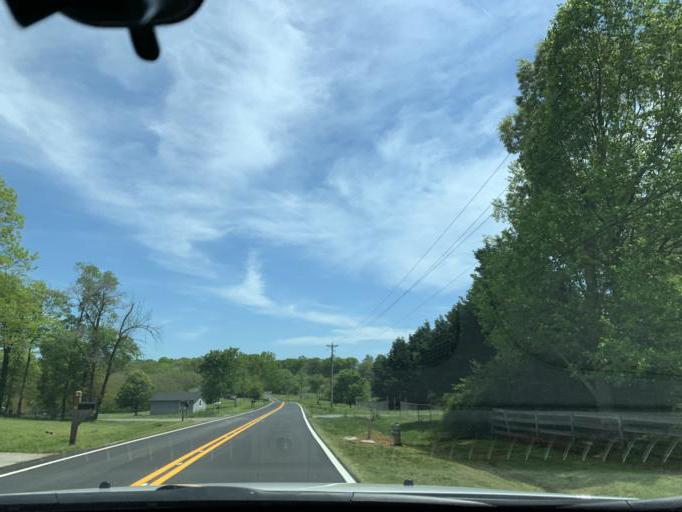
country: US
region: Georgia
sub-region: Forsyth County
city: Cumming
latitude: 34.2590
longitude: -84.0284
